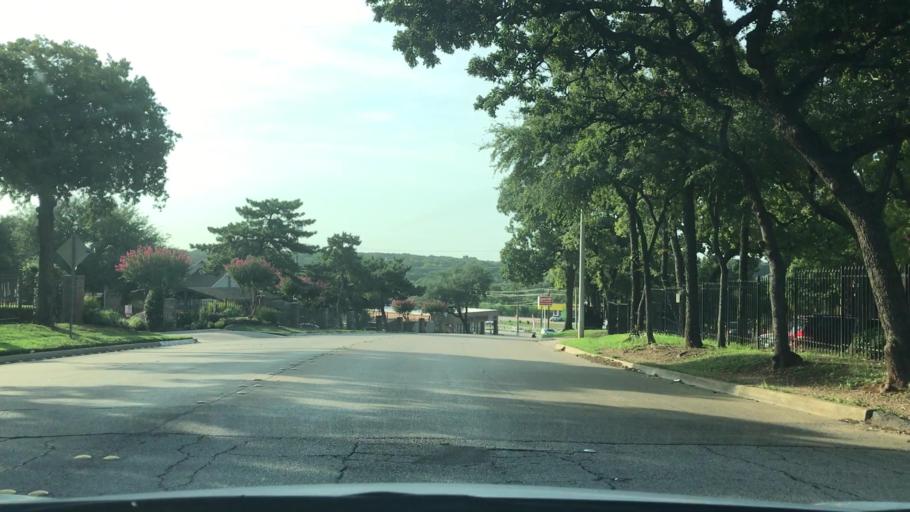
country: US
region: Texas
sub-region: Tarrant County
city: Pantego
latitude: 32.7593
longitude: -97.1574
